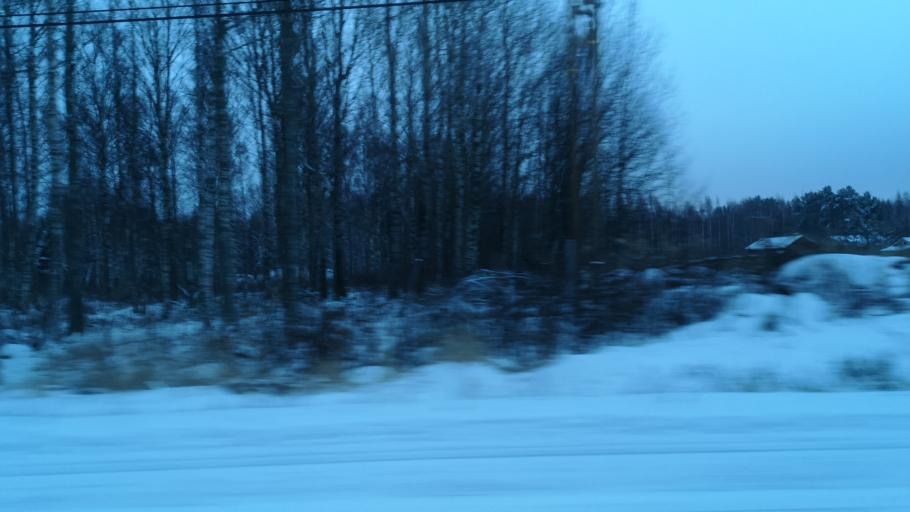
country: FI
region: Southern Savonia
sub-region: Savonlinna
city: Enonkoski
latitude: 62.0675
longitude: 28.7367
